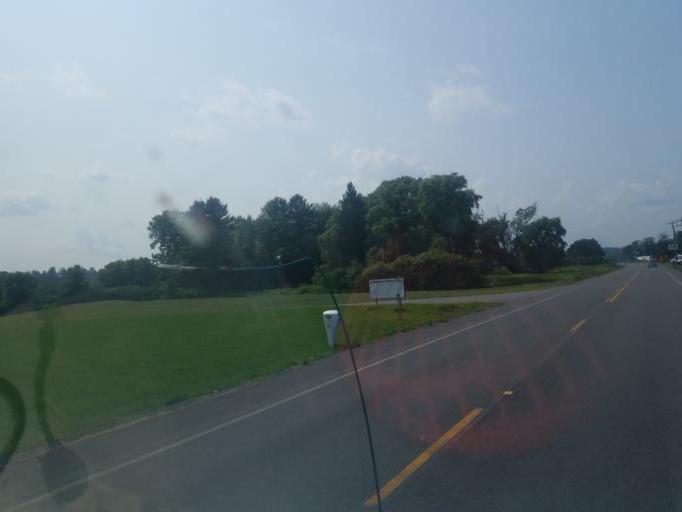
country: US
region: New York
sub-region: Montgomery County
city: Fonda
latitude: 42.9469
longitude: -74.3530
